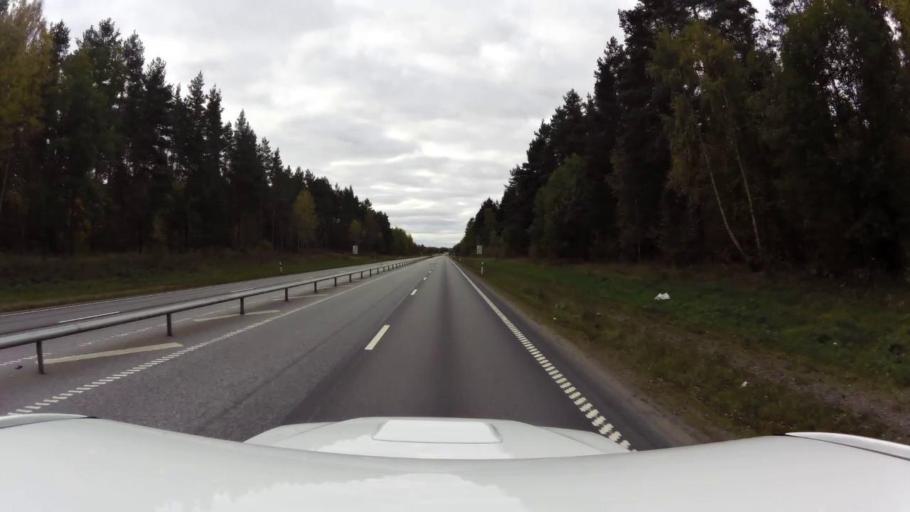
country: SE
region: OEstergoetland
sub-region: Linkopings Kommun
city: Malmslatt
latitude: 58.3764
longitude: 15.5428
